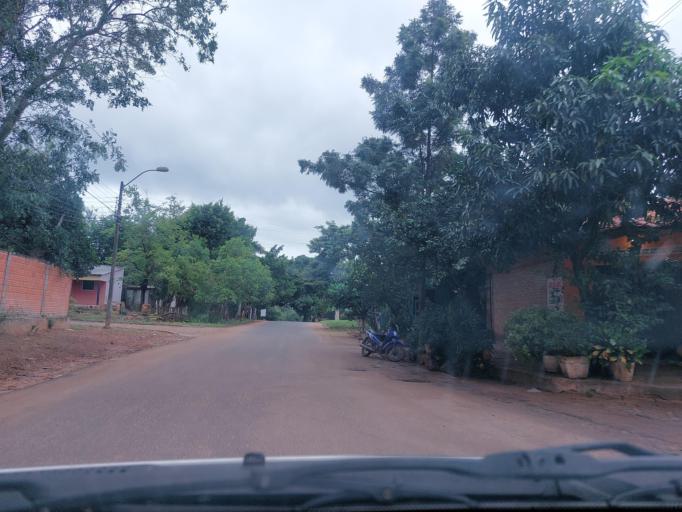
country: PY
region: San Pedro
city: Guayaybi
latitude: -24.6753
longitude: -56.4482
